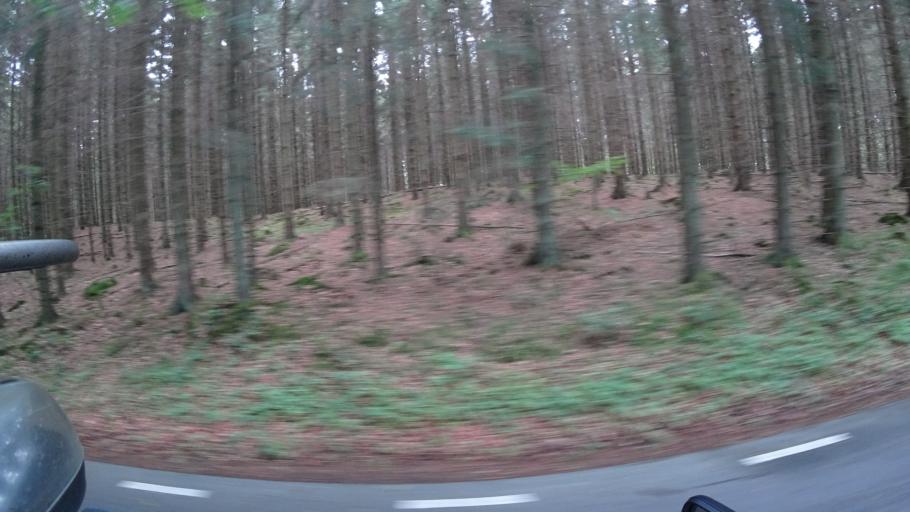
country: SE
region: Skane
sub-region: Kristianstads Kommun
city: Degeberga
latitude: 55.7272
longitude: 13.9562
